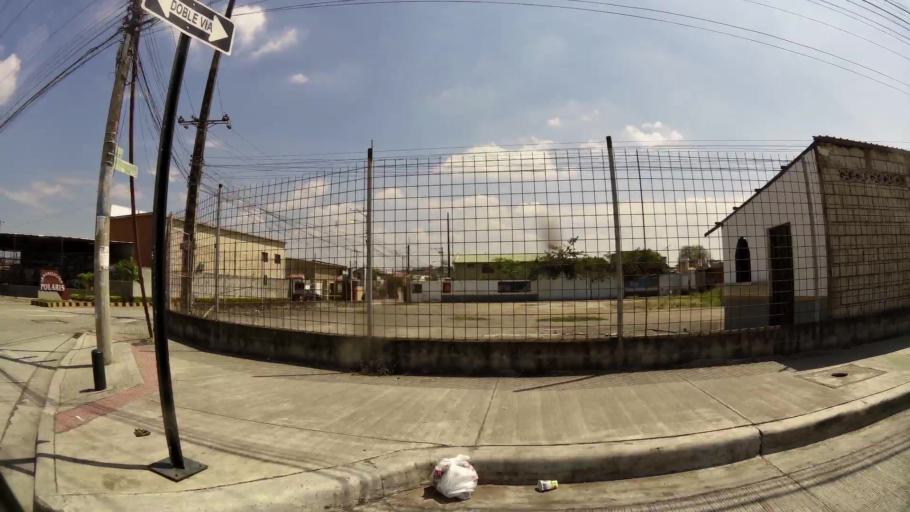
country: EC
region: Guayas
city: Eloy Alfaro
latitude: -2.1174
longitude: -79.9000
